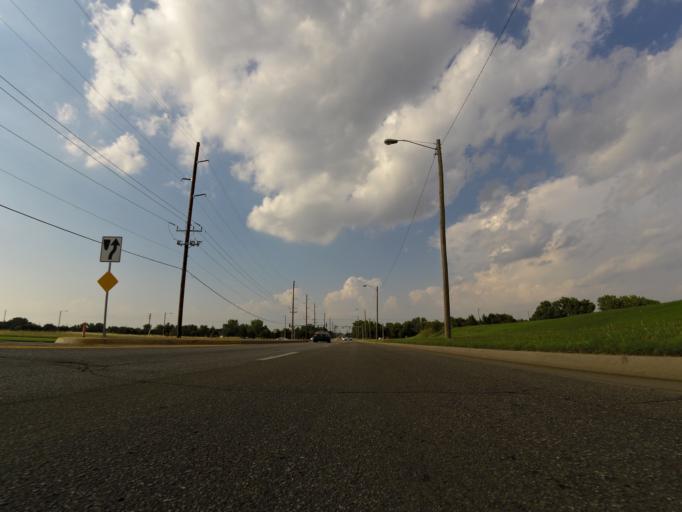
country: US
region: Kansas
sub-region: Sedgwick County
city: Bellaire
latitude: 37.7361
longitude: -97.2623
